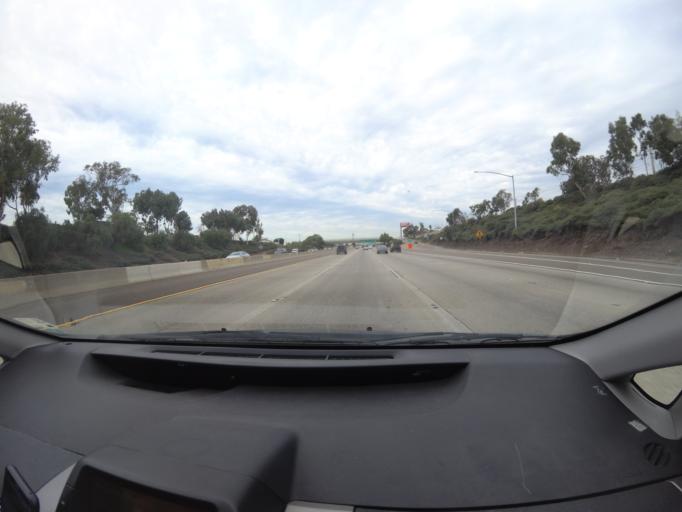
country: US
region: California
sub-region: San Diego County
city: Chula Vista
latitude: 32.6367
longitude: -117.0988
